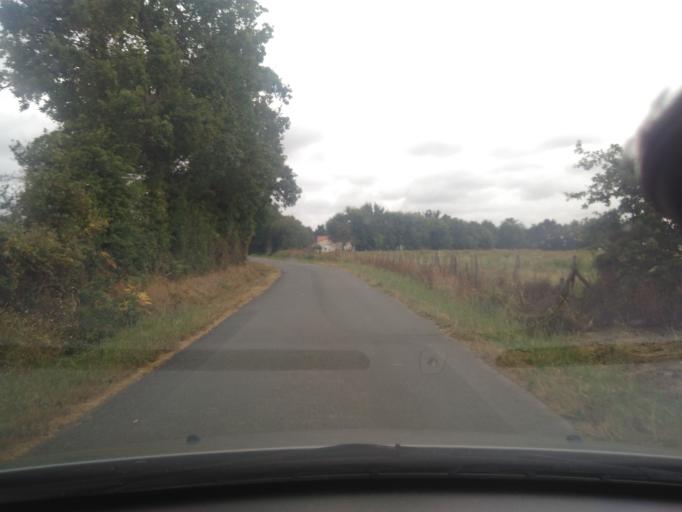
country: FR
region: Pays de la Loire
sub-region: Departement de la Vendee
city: La Ferriere
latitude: 46.7089
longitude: -1.3003
